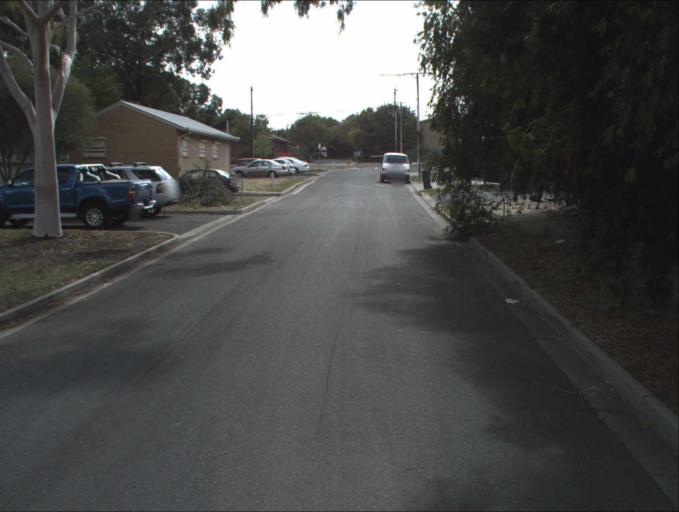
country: AU
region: South Australia
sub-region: Port Adelaide Enfield
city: Gilles Plains
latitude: -34.8541
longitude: 138.6600
